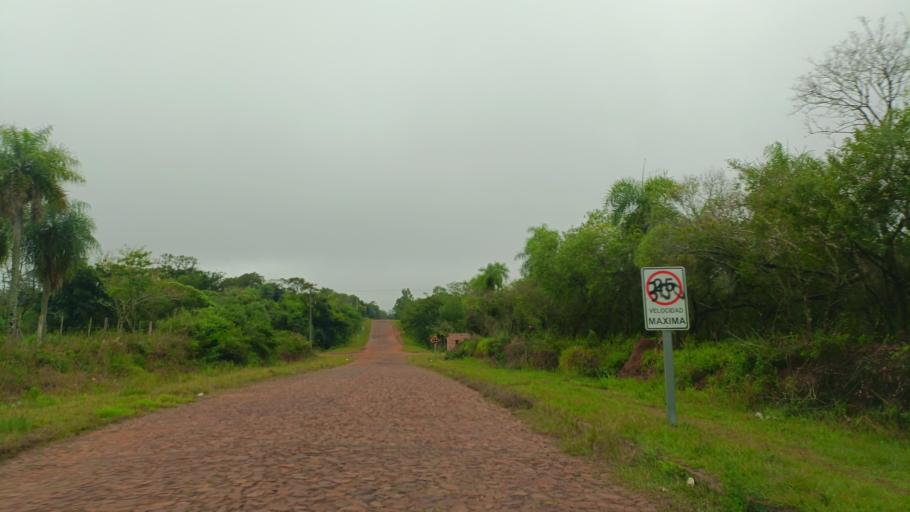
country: PY
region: Misiones
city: Santa Maria
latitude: -26.8733
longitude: -57.0121
